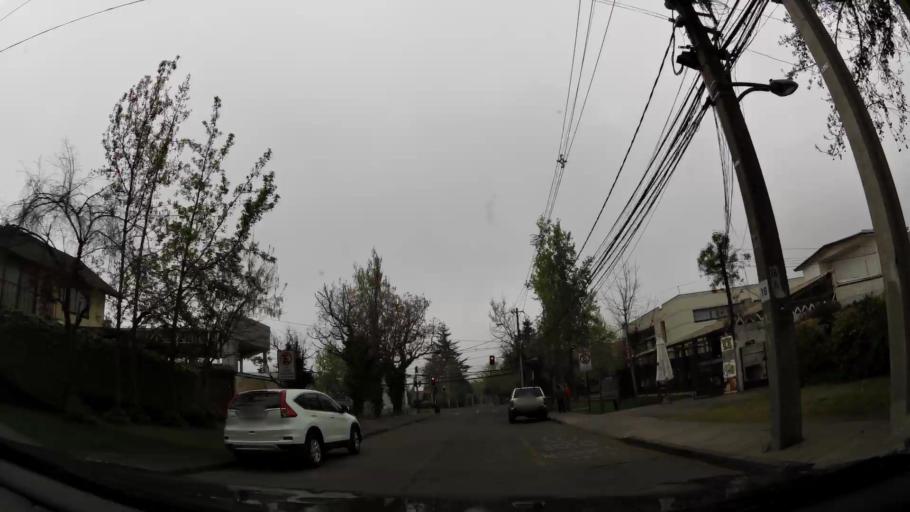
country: CL
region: Santiago Metropolitan
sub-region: Provincia de Santiago
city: Villa Presidente Frei, Nunoa, Santiago, Chile
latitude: -33.3849
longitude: -70.5563
